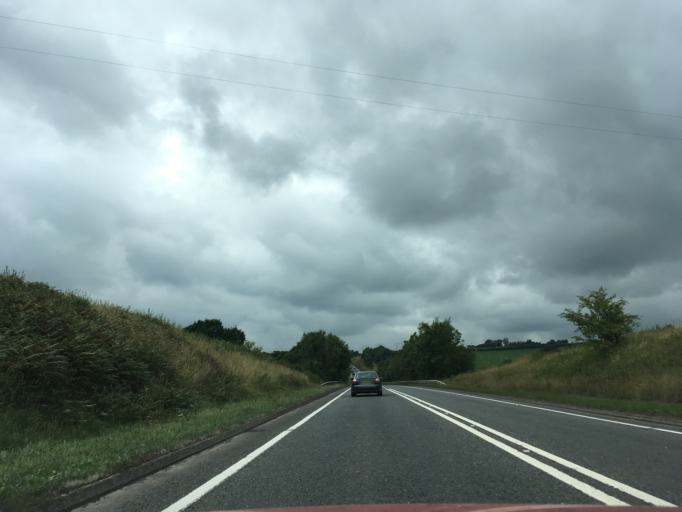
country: GB
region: Wales
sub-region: Carmarthenshire
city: Whitland
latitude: 51.8238
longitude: -4.5816
